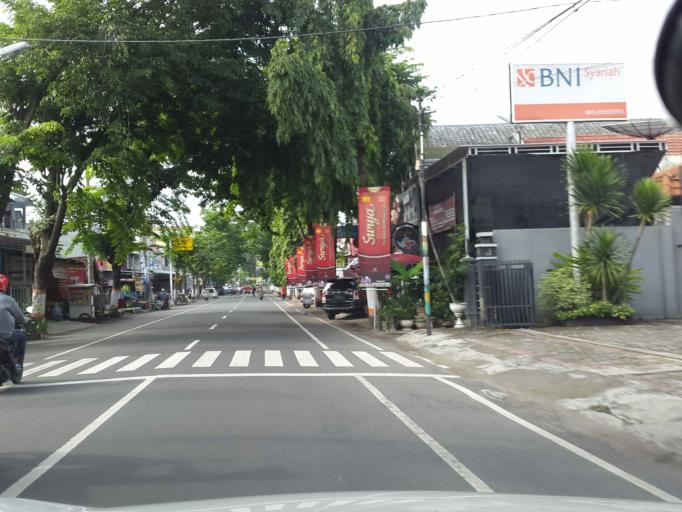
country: ID
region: East Java
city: Soko
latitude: -7.4778
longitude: 112.4320
